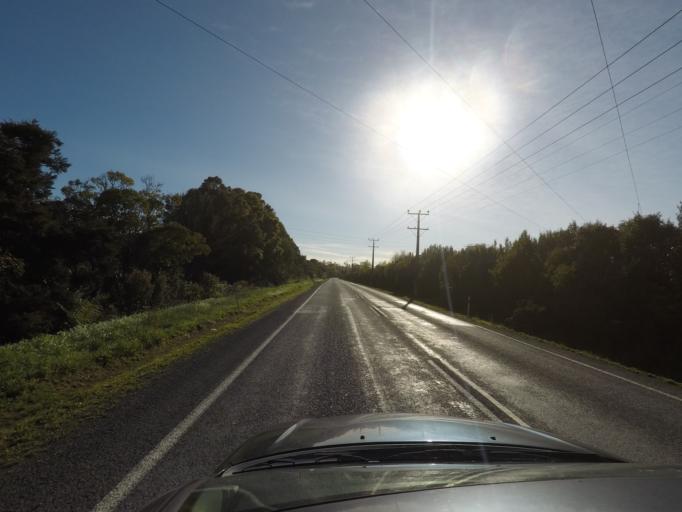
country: NZ
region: Auckland
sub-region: Auckland
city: Red Hill
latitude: -36.9998
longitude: 174.9649
